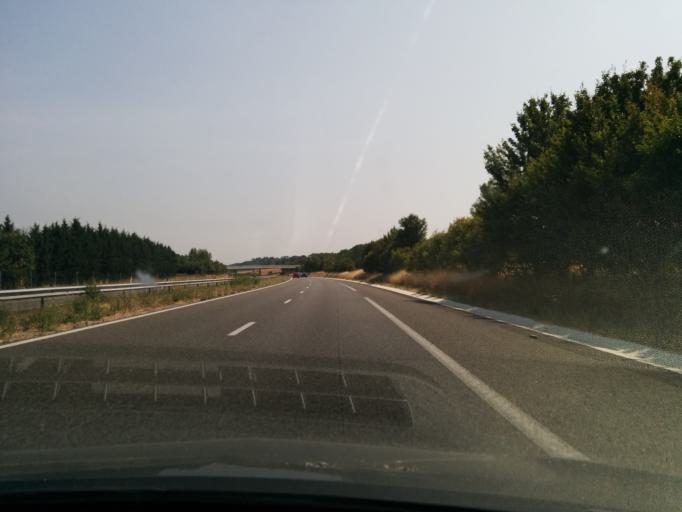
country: FR
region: Midi-Pyrenees
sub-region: Departement du Tarn
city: Lisle-sur-Tarn
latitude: 43.8157
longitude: 1.8078
